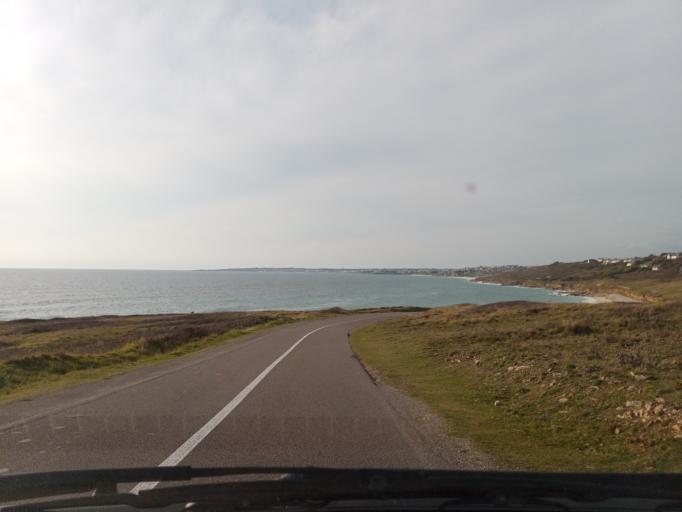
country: FR
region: Brittany
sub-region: Departement du Finistere
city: Plouhinec
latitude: 47.9888
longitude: -4.4767
